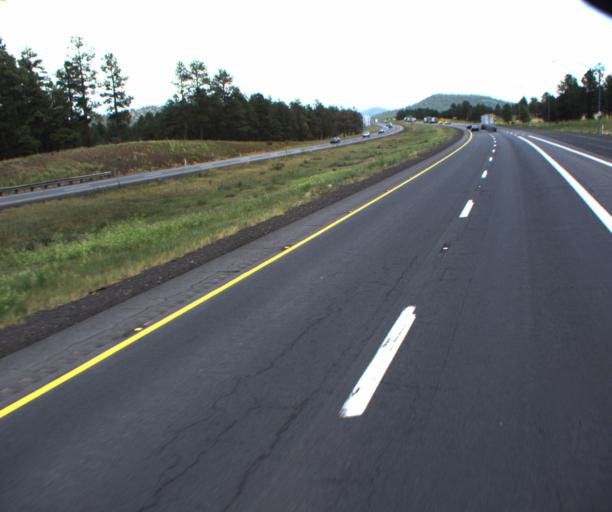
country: US
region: Arizona
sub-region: Coconino County
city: Williams
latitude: 35.2583
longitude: -112.1451
